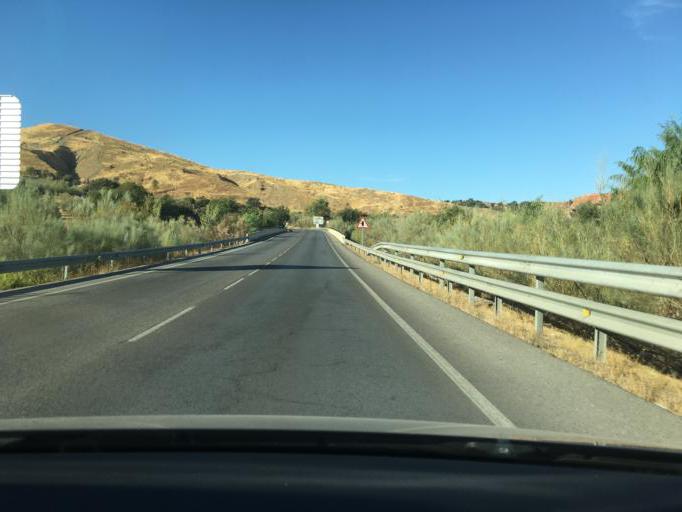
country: ES
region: Andalusia
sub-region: Provincia de Granada
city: Cenes de la Vega
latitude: 37.1557
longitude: -3.5317
